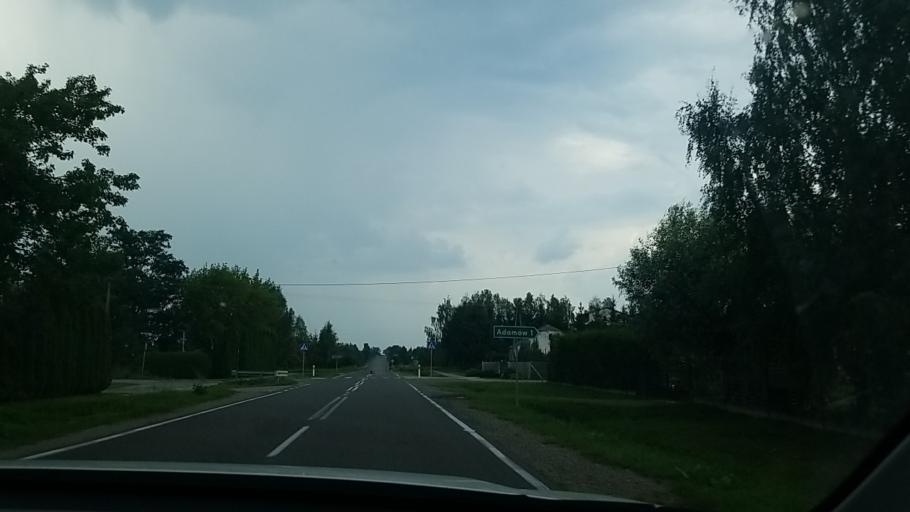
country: PL
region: Lublin Voivodeship
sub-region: Powiat leczynski
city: Cycow
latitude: 51.2534
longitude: 23.0922
